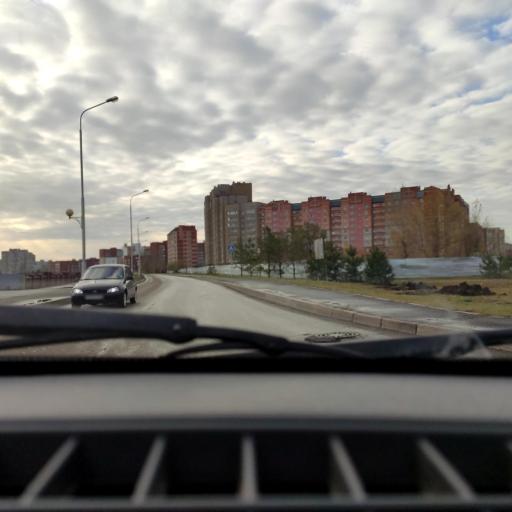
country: RU
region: Bashkortostan
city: Ufa
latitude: 54.7823
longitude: 56.0772
